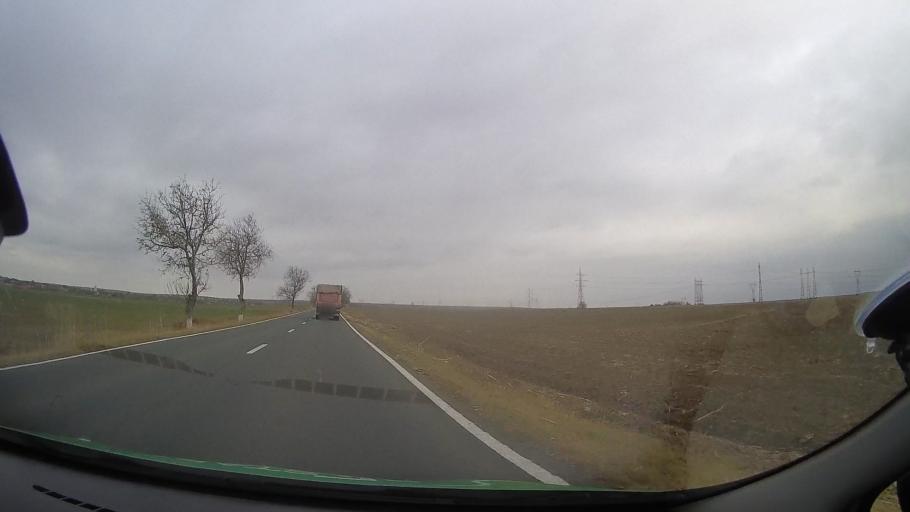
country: RO
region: Constanta
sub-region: Comuna Castelu
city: Castelu
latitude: 44.2548
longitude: 28.3521
